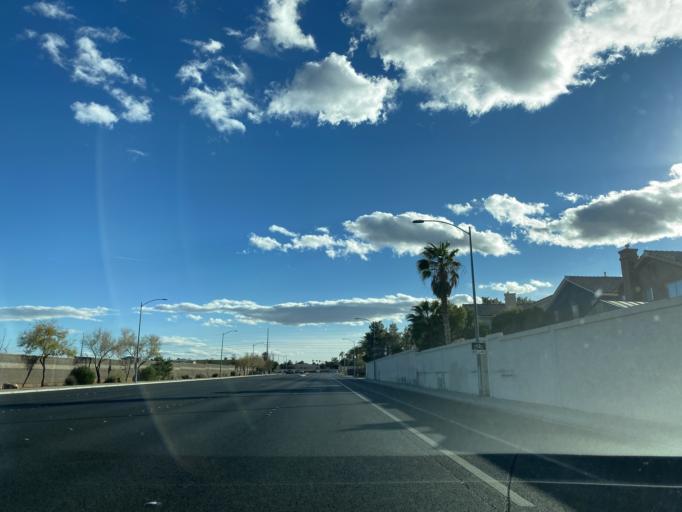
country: US
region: Nevada
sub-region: Clark County
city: Summerlin South
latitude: 36.2215
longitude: -115.2974
